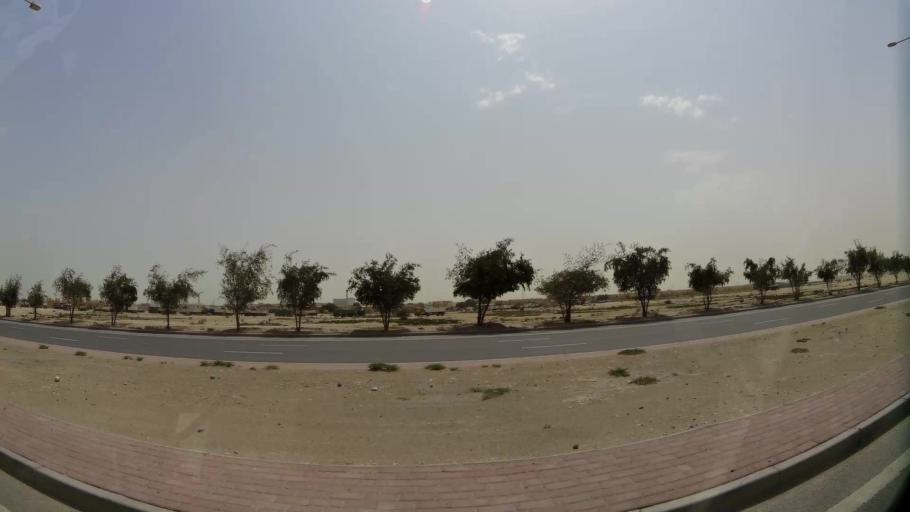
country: QA
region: Baladiyat ar Rayyan
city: Ar Rayyan
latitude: 25.2416
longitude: 51.4125
